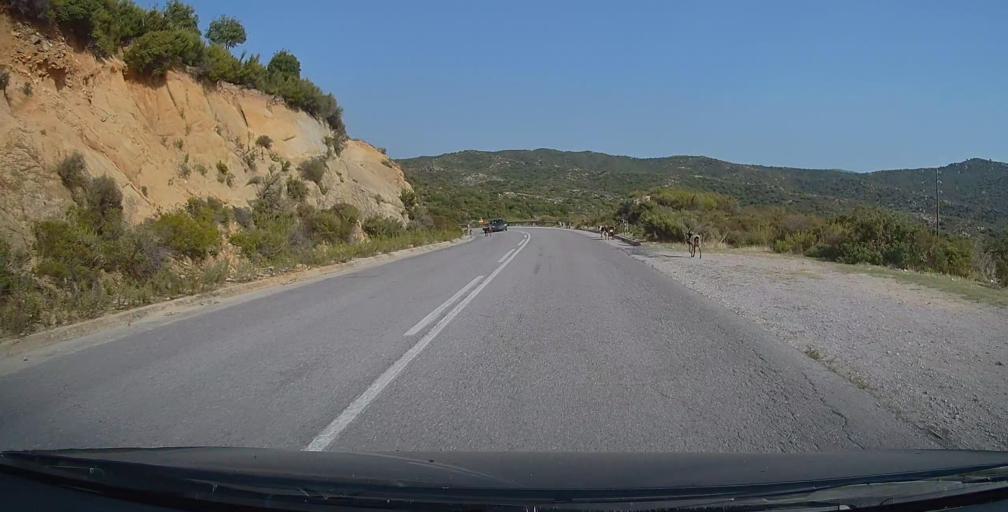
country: GR
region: Central Macedonia
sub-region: Nomos Chalkidikis
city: Sykia
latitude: 39.9894
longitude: 23.9575
